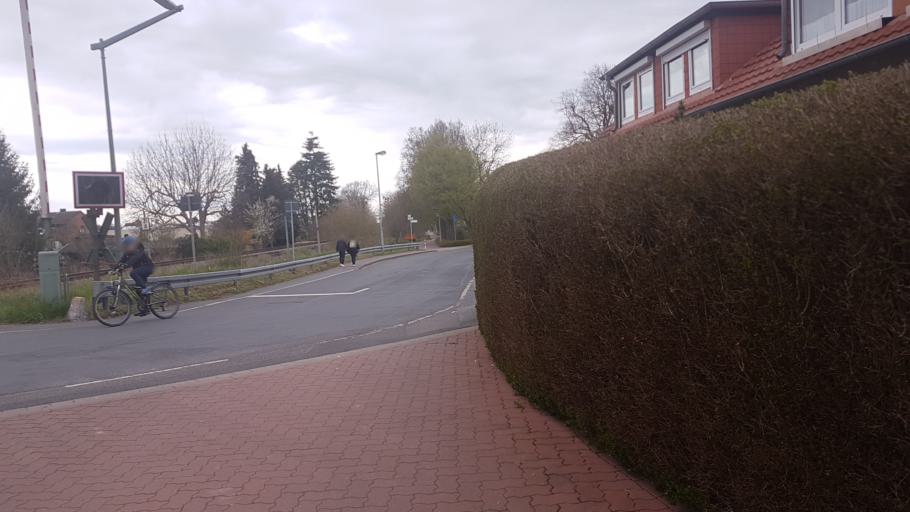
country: DE
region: Lower Saxony
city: Hameln
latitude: 52.1160
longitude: 9.3517
